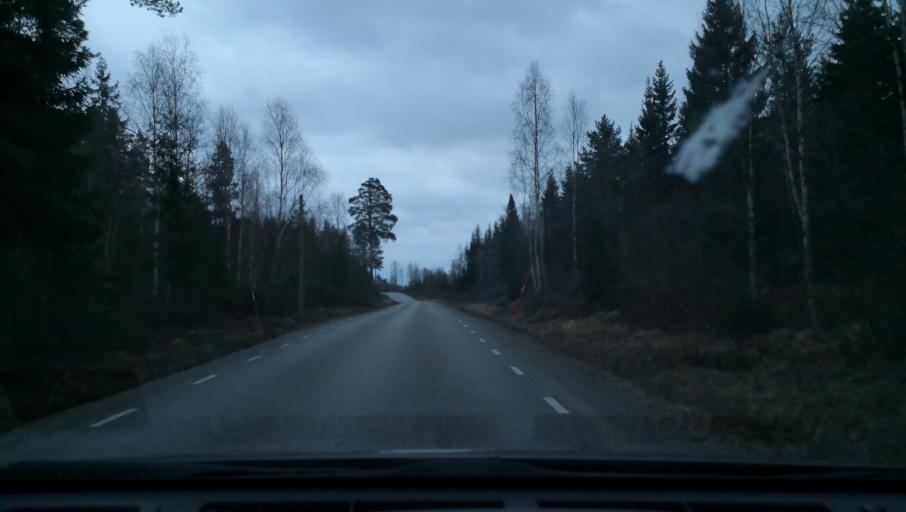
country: SE
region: OErebro
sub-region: Lindesbergs Kommun
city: Fellingsbro
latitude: 59.5696
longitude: 15.5740
